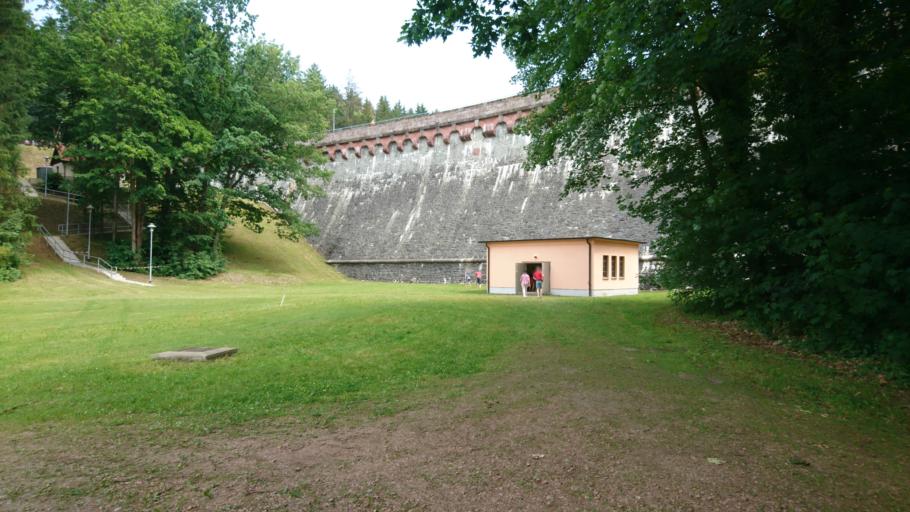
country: DE
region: Saxony
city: Gornau
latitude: 50.7753
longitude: 12.9803
